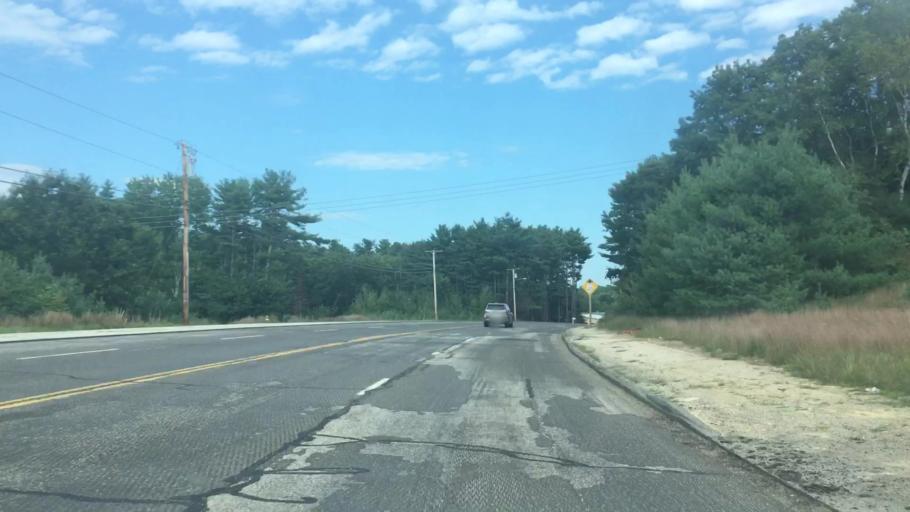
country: US
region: Maine
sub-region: Androscoggin County
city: Minot
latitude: 44.0802
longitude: -70.2848
